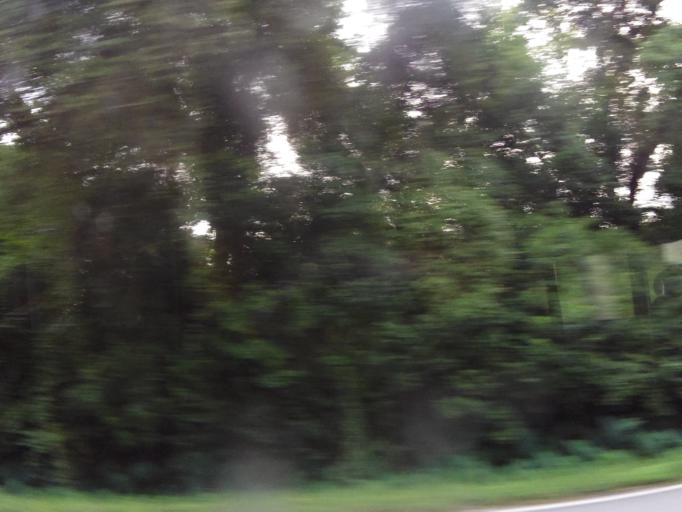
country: US
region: Florida
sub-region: Clay County
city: Bellair-Meadowbrook Terrace
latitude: 30.2647
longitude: -81.7812
